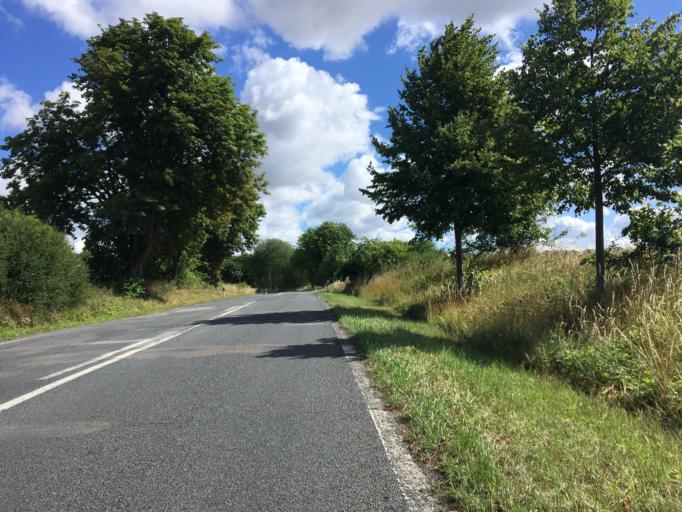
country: DE
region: Brandenburg
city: Mittenwalde
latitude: 53.1865
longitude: 13.5877
